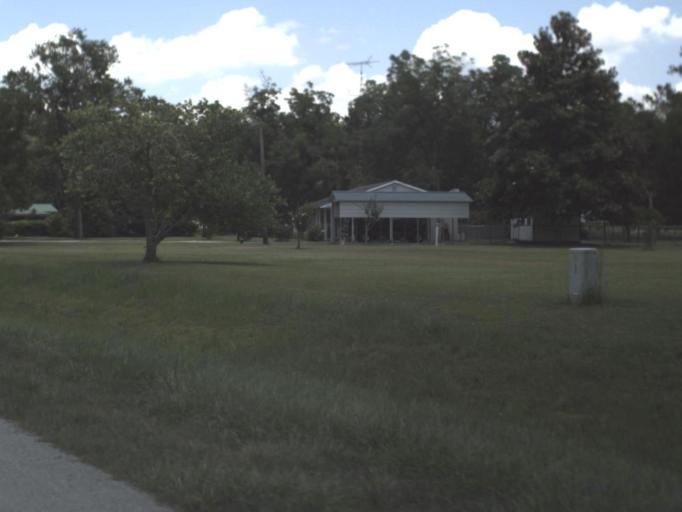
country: US
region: Florida
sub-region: Bradford County
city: Starke
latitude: 30.0104
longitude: -82.1421
